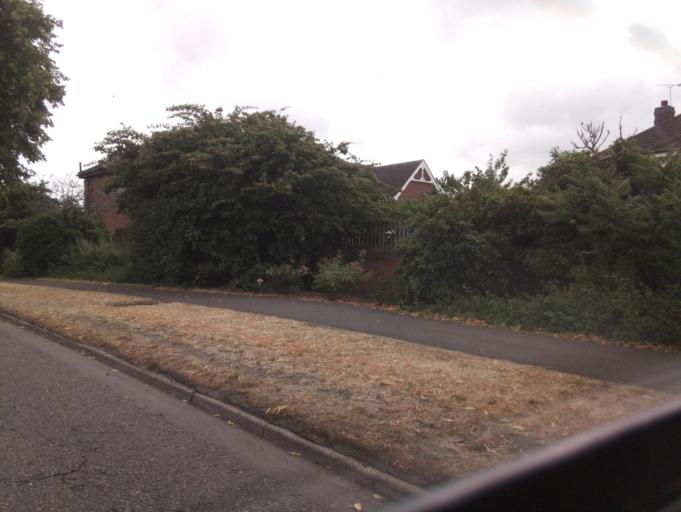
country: GB
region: England
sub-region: Derbyshire
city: Long Eaton
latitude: 52.8979
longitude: -1.2936
